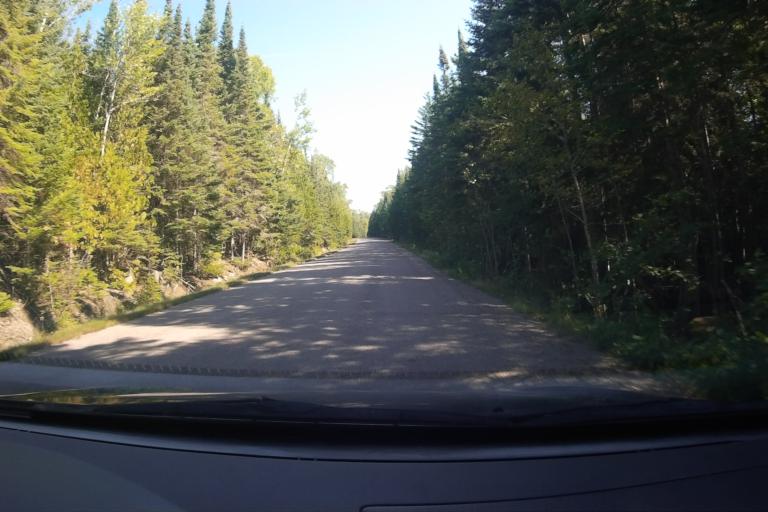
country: CA
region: Ontario
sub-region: Thunder Bay District
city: Thunder Bay
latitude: 48.3449
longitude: -88.8114
